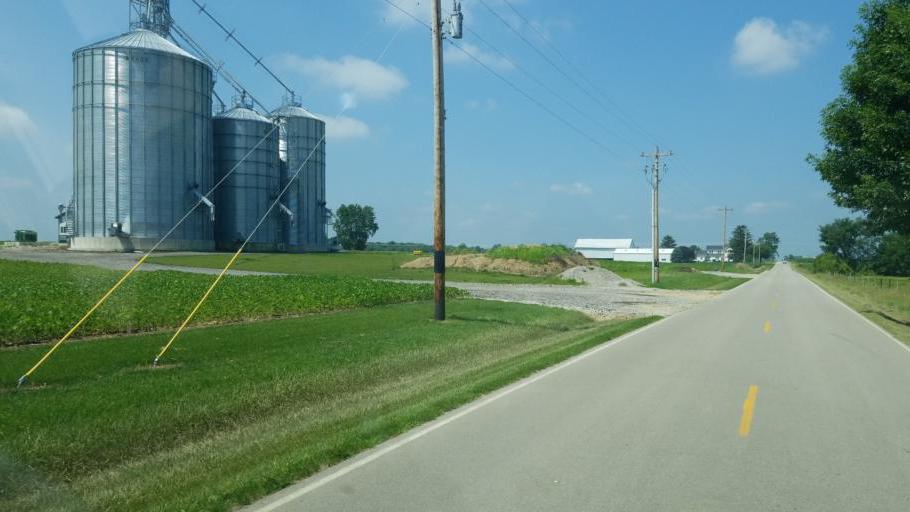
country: US
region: Ohio
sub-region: Crawford County
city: Bucyrus
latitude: 40.9937
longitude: -82.9732
